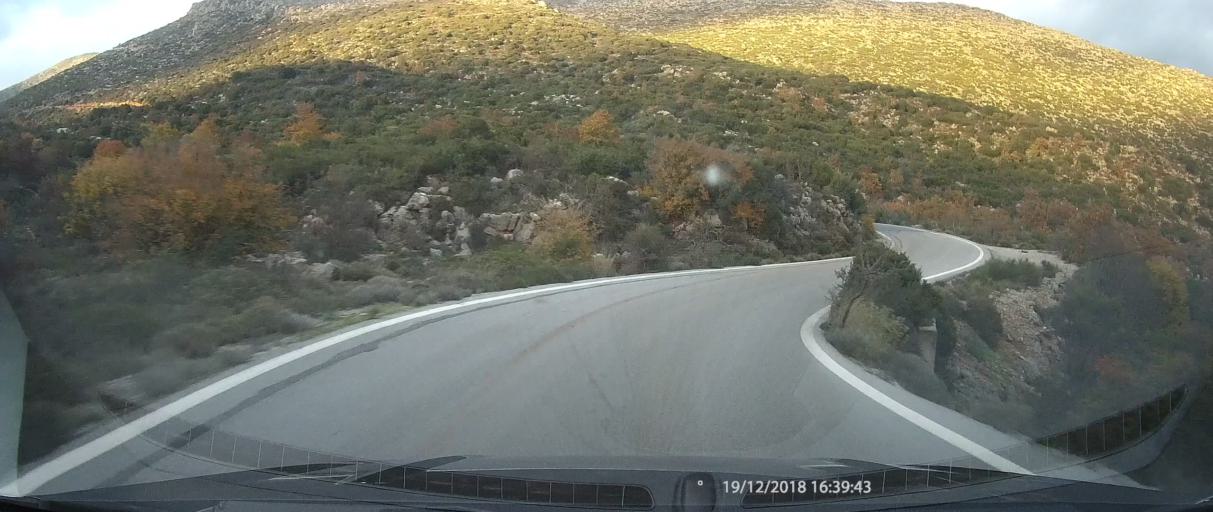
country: GR
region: Peloponnese
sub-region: Nomos Lakonias
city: Sykea
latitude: 36.9014
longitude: 22.9787
